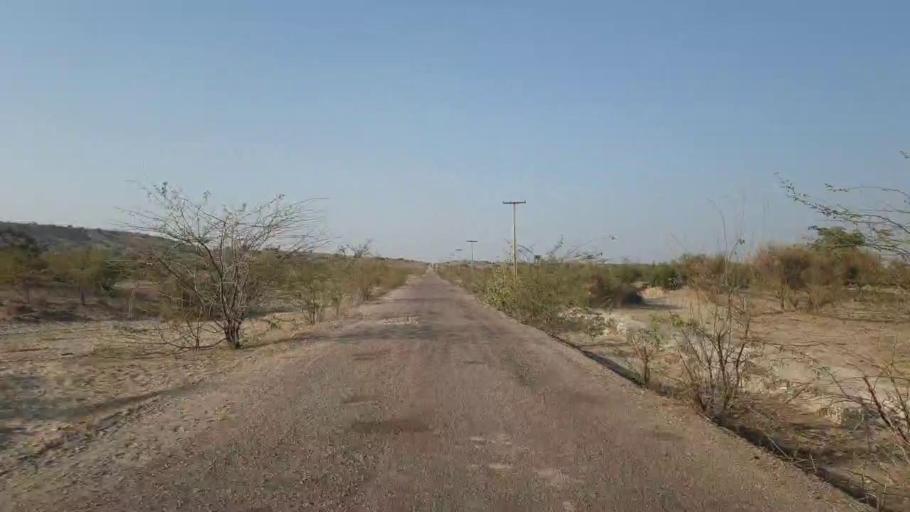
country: PK
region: Sindh
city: Chor
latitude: 25.6014
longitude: 69.8379
